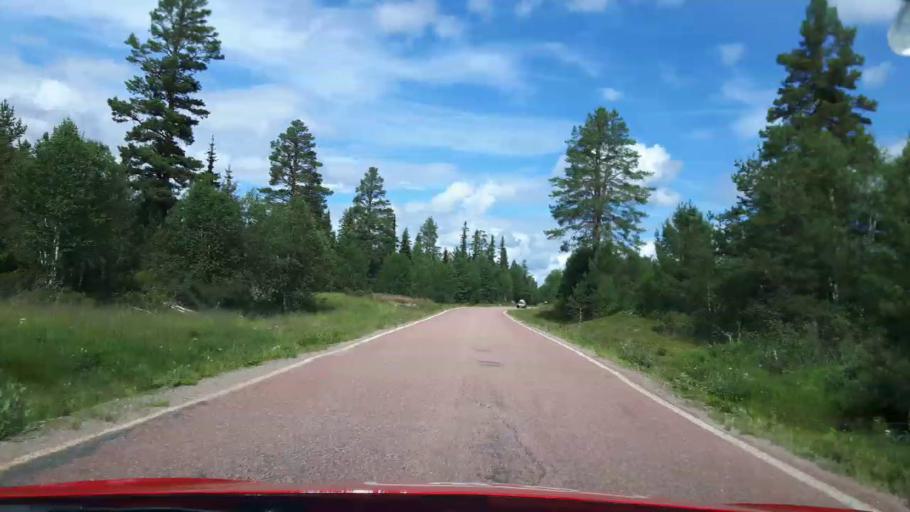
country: NO
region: Hedmark
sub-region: Trysil
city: Innbygda
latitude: 62.0158
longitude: 12.9779
